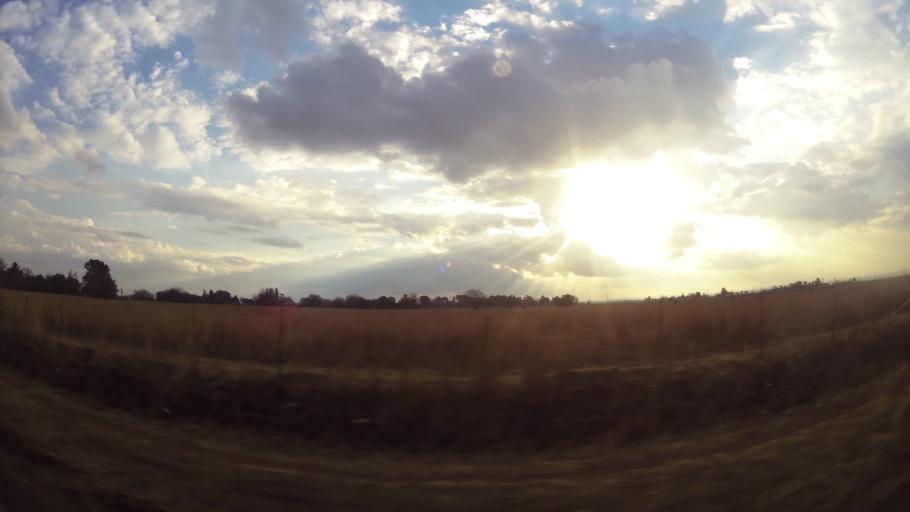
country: ZA
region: Gauteng
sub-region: Sedibeng District Municipality
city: Vanderbijlpark
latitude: -26.6349
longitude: 27.8076
